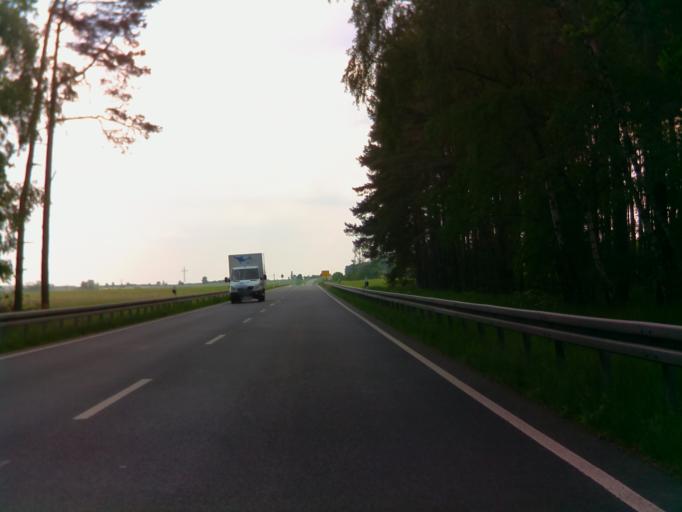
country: DE
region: Saxony-Anhalt
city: Schollene
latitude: 52.5784
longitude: 12.2333
